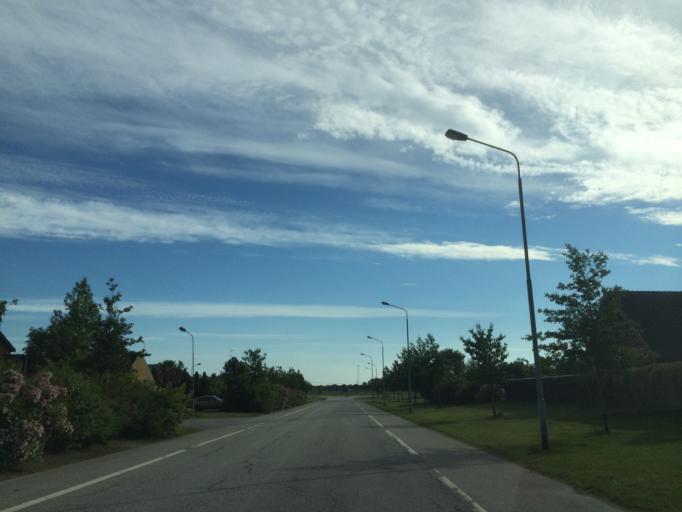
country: SE
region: Skane
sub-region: Staffanstorps Kommun
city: Hjaerup
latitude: 55.6679
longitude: 13.1372
